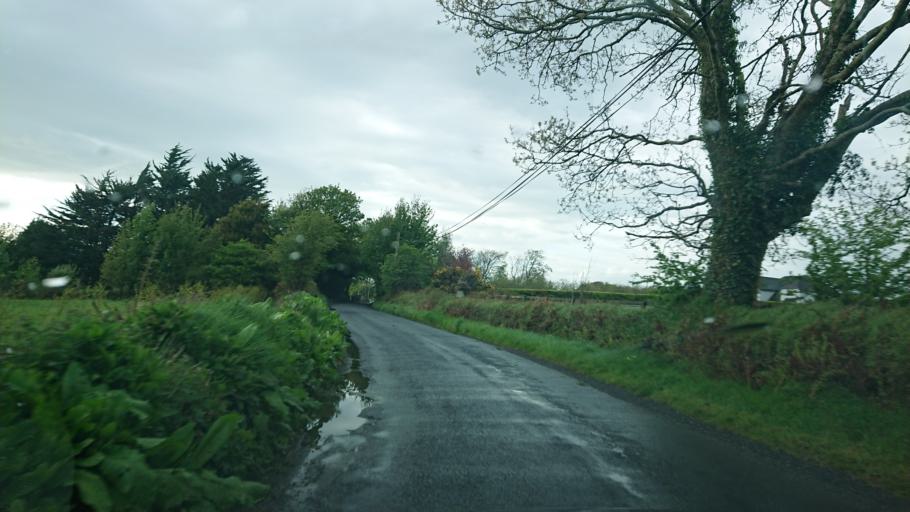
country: IE
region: Munster
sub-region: Waterford
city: Waterford
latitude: 52.2301
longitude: -7.0732
